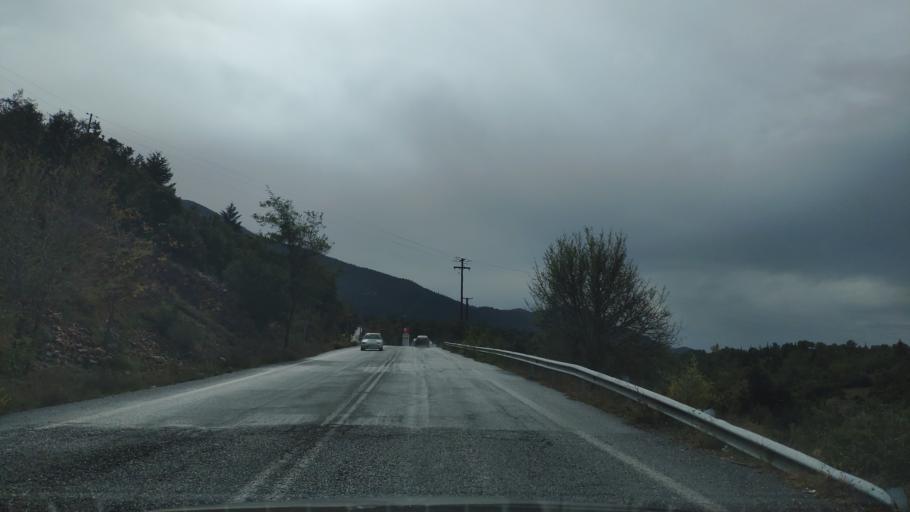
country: GR
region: Peloponnese
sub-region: Nomos Arkadias
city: Langadhia
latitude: 37.6830
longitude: 22.1911
